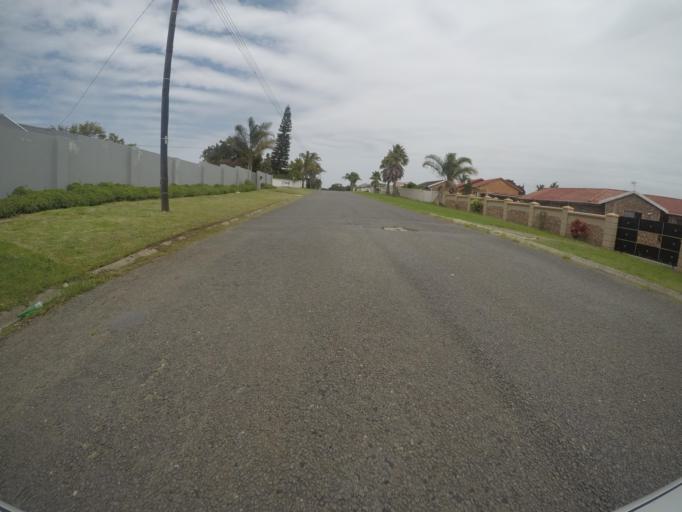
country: ZA
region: Eastern Cape
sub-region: Buffalo City Metropolitan Municipality
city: East London
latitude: -32.9615
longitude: 27.9311
